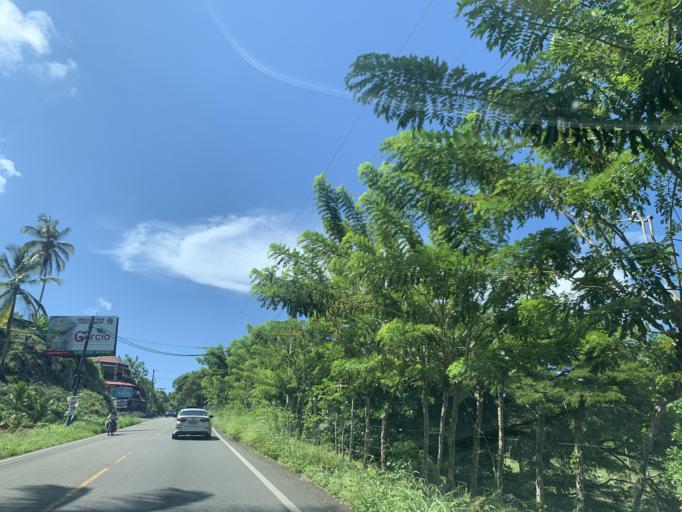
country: DO
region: Maria Trinidad Sanchez
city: Cabrera
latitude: 19.6492
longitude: -69.9287
